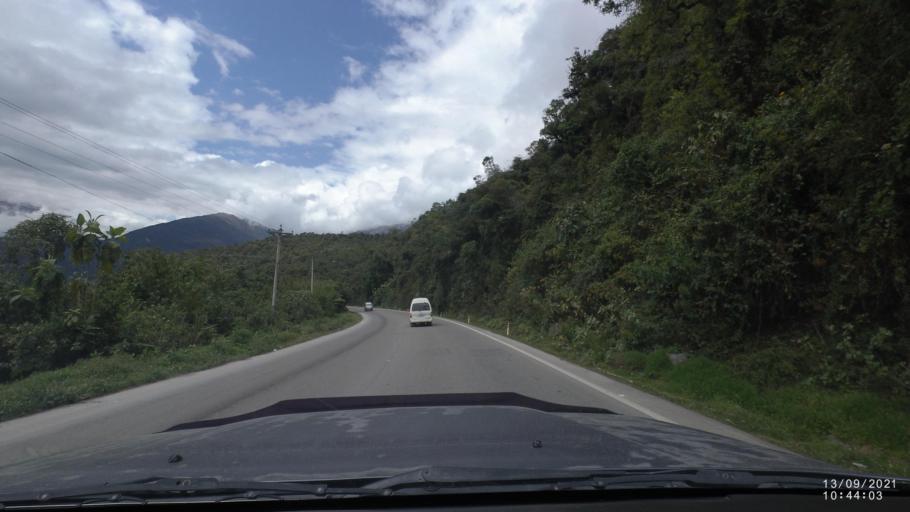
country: BO
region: Cochabamba
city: Colomi
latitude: -17.1903
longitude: -65.8823
